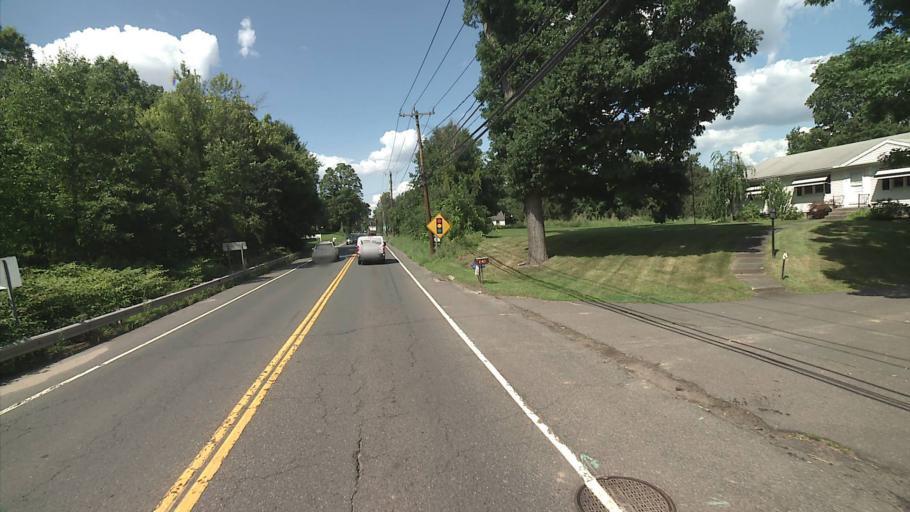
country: US
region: Connecticut
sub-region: Hartford County
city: Thompsonville
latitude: 41.9951
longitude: -72.6139
